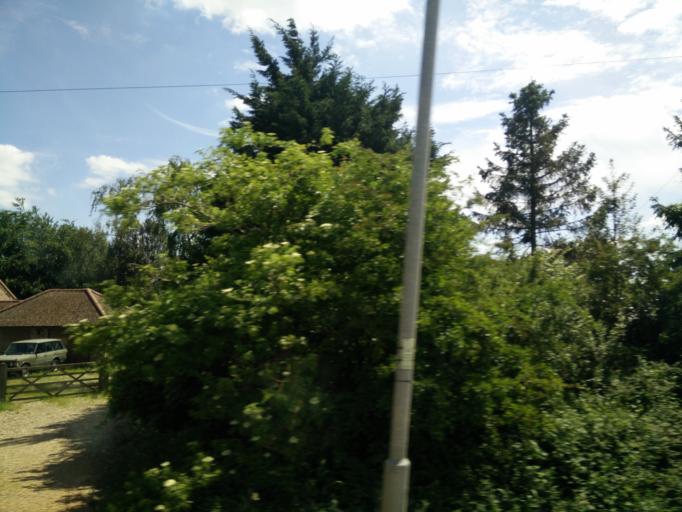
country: GB
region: England
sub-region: Cambridgeshire
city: Grantchester
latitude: 52.1680
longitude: 0.1099
